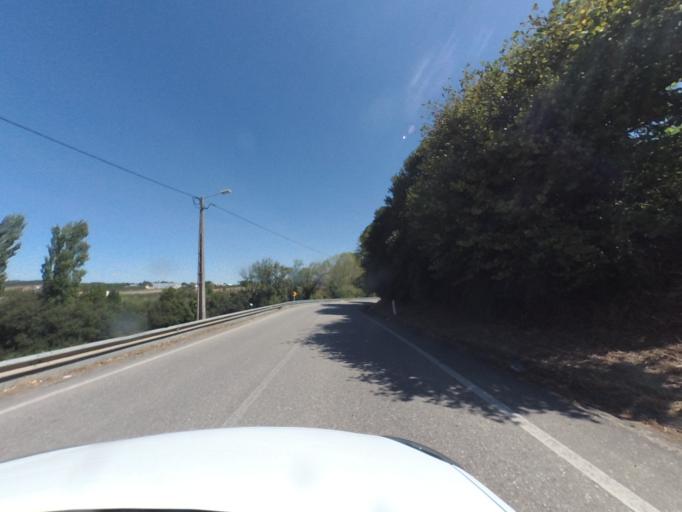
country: PT
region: Leiria
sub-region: Alcobaca
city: Alcobaca
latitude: 39.5212
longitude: -9.0151
